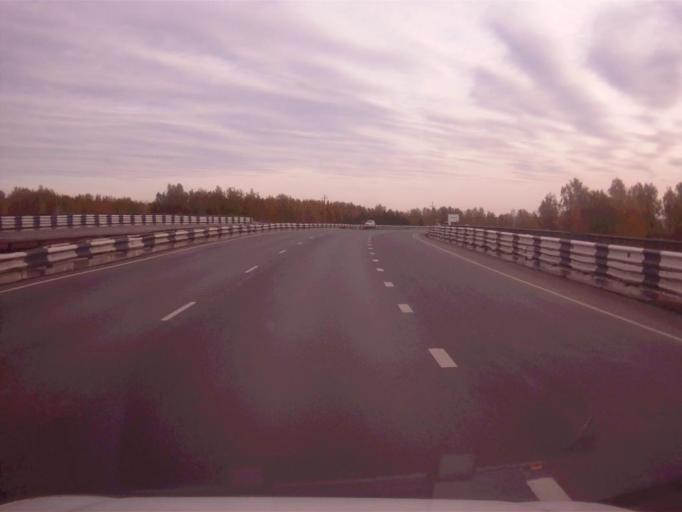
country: RU
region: Chelyabinsk
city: Novosineglazovskiy
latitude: 55.0398
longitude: 61.4394
